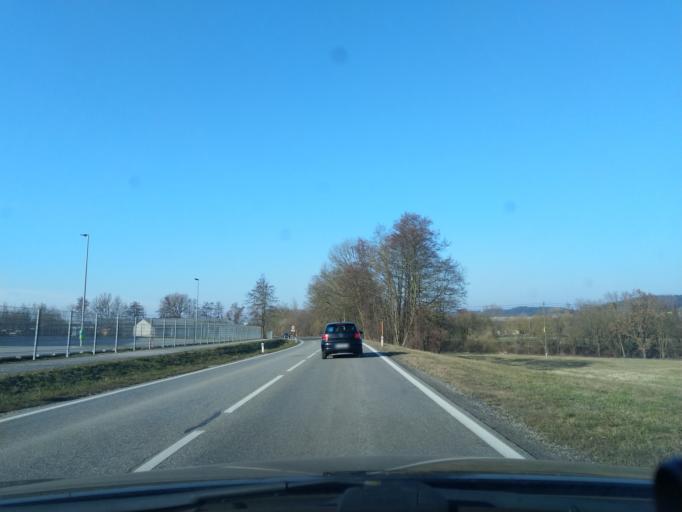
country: AT
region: Upper Austria
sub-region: Politischer Bezirk Scharding
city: Sankt Marienkirchen bei Schaerding
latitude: 48.3061
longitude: 13.4274
